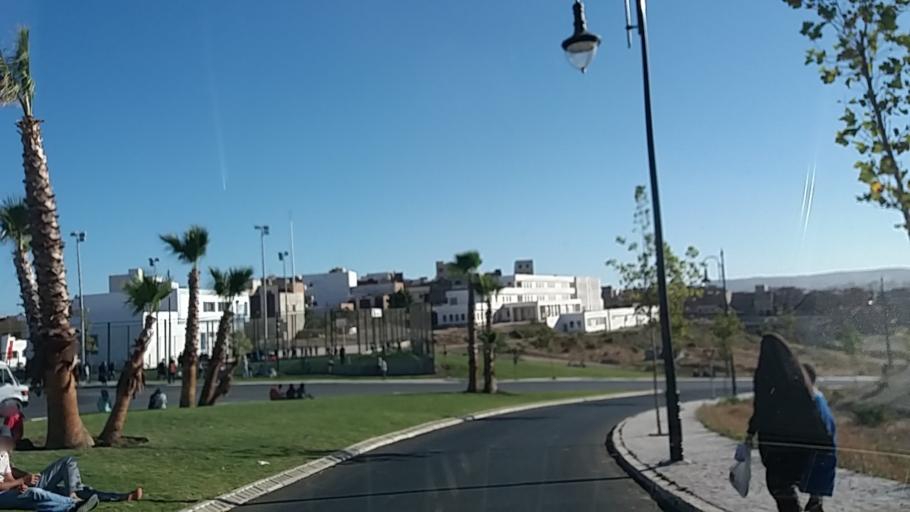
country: MA
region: Tanger-Tetouan
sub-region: Tanger-Assilah
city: Tangier
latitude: 35.7298
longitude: -5.7877
